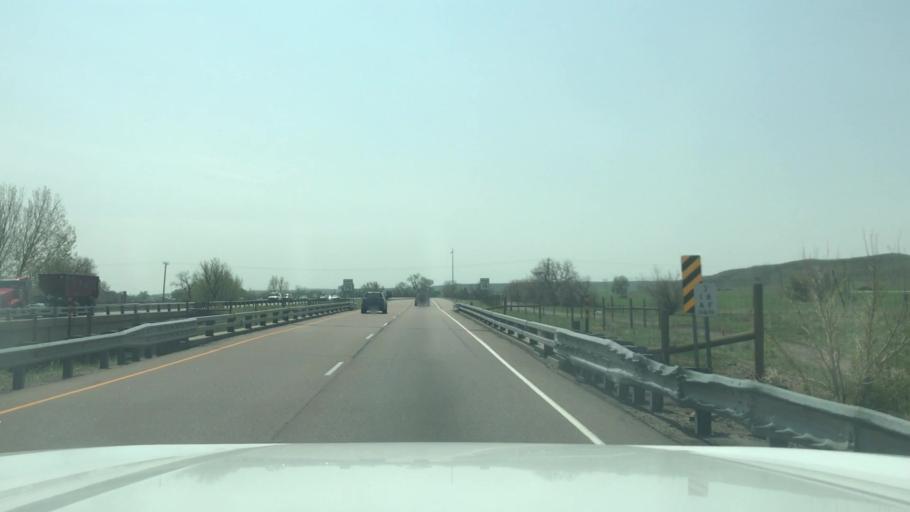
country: US
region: Colorado
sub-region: El Paso County
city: Fountain
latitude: 38.6215
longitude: -104.6893
